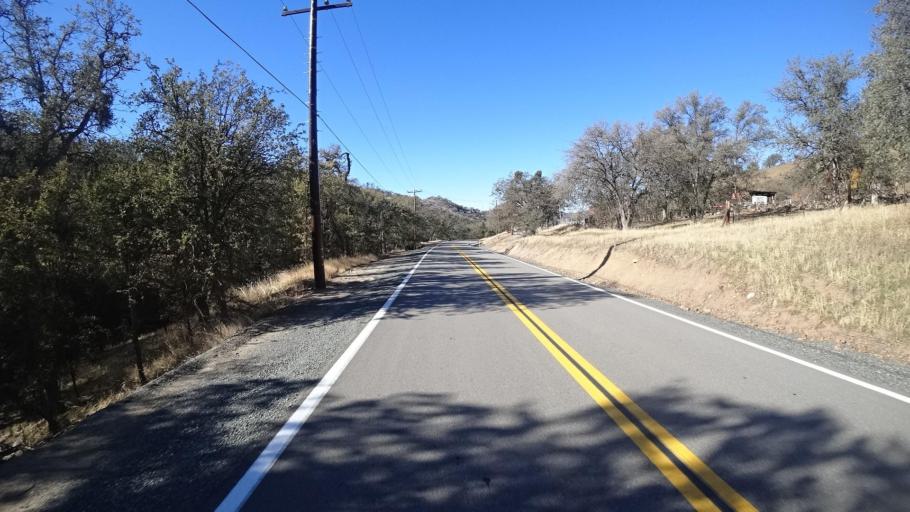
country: US
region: California
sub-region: Kern County
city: Alta Sierra
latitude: 35.7210
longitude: -118.6881
